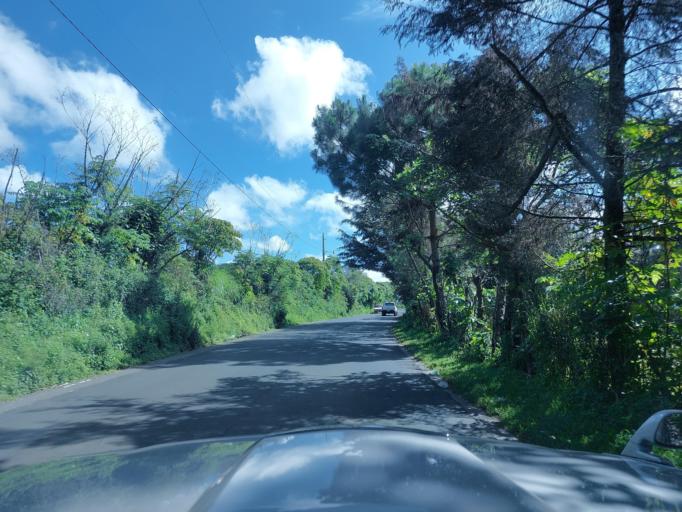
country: GT
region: Chimaltenango
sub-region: Municipio de Zaragoza
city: Zaragoza
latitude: 14.6527
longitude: -90.8975
